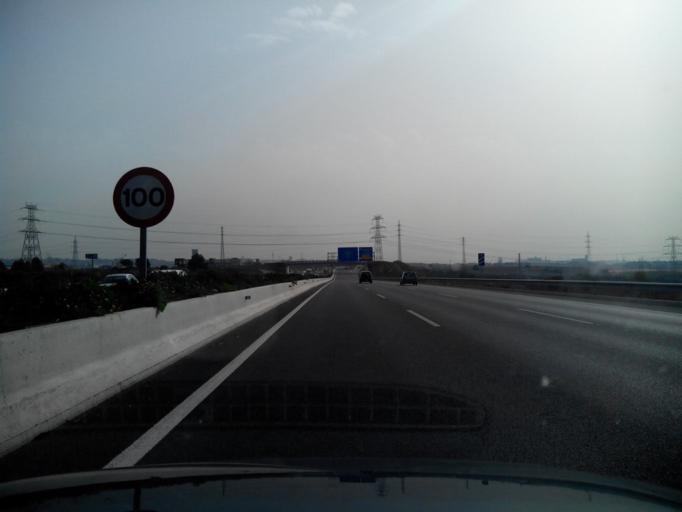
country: ES
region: Catalonia
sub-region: Provincia de Tarragona
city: Constanti
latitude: 41.1309
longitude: 1.1915
